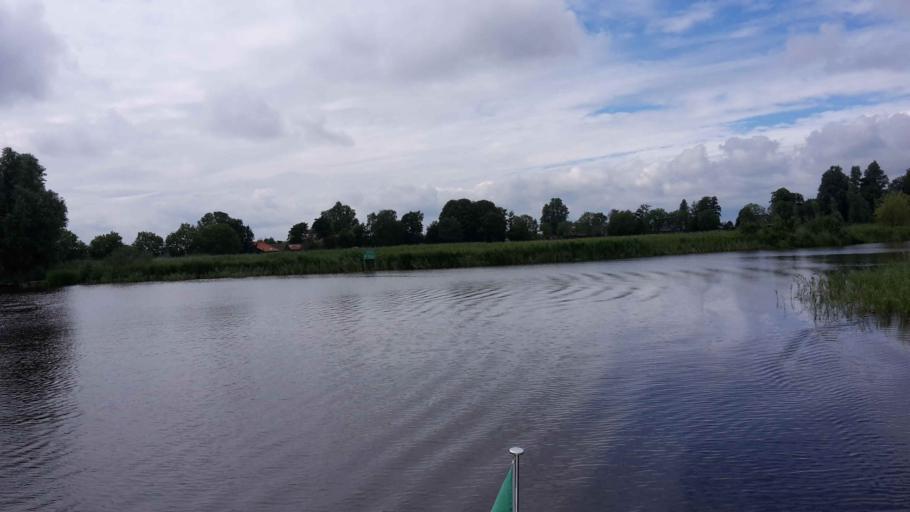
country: NL
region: Friesland
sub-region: Gemeente Lemsterland
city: Echtenerbrug
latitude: 52.8678
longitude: 5.8577
